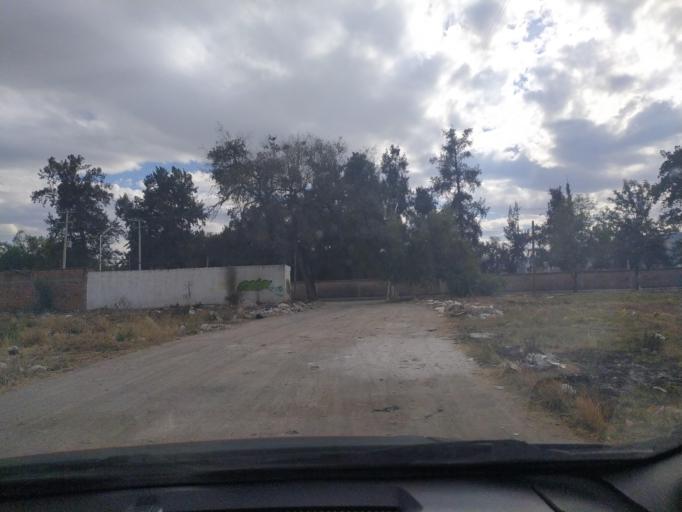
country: LA
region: Oudomxai
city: Muang La
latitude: 21.0220
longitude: 101.8642
